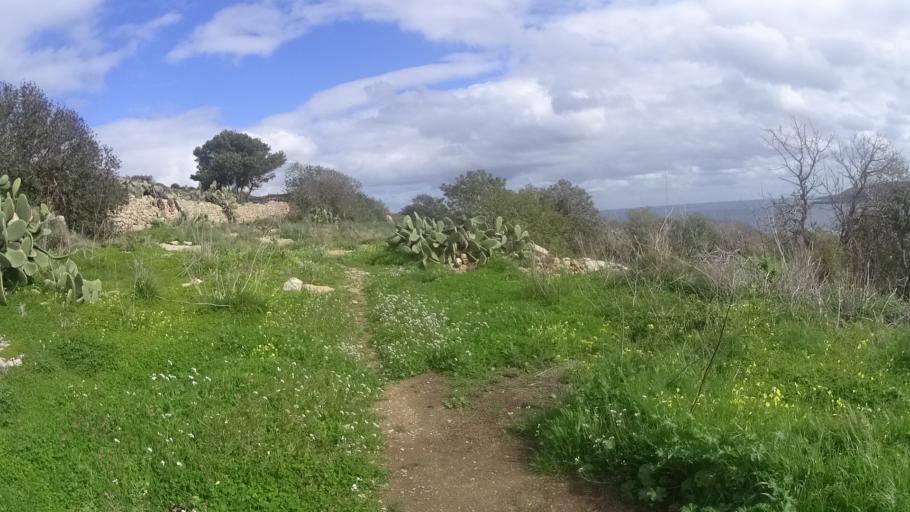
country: MT
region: Il-Mellieha
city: Mellieha
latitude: 35.9769
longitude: 14.3518
